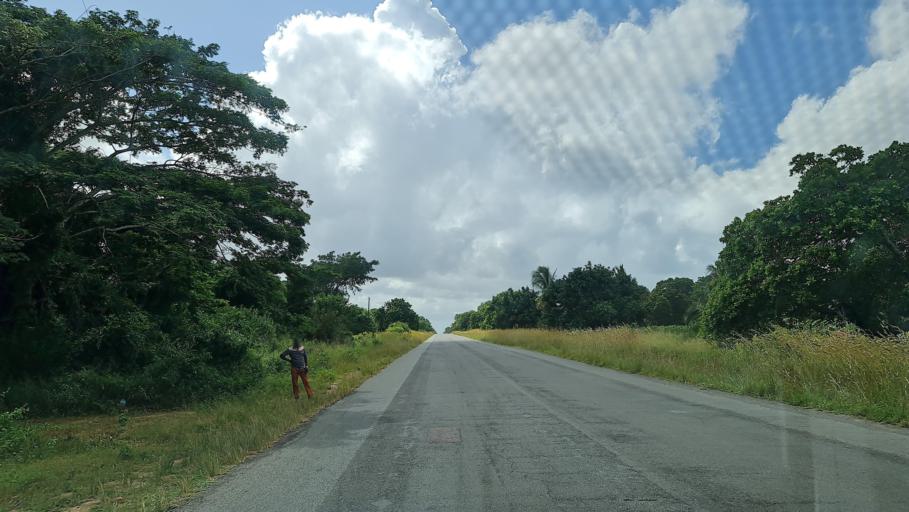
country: MZ
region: Gaza
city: Manjacaze
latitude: -24.6786
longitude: 34.5968
